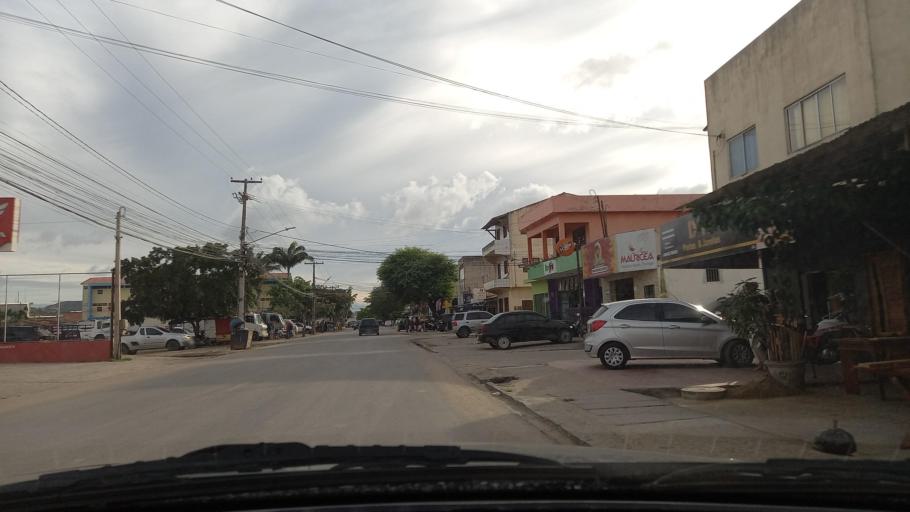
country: BR
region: Pernambuco
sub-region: Gravata
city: Gravata
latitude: -8.1971
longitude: -35.5585
